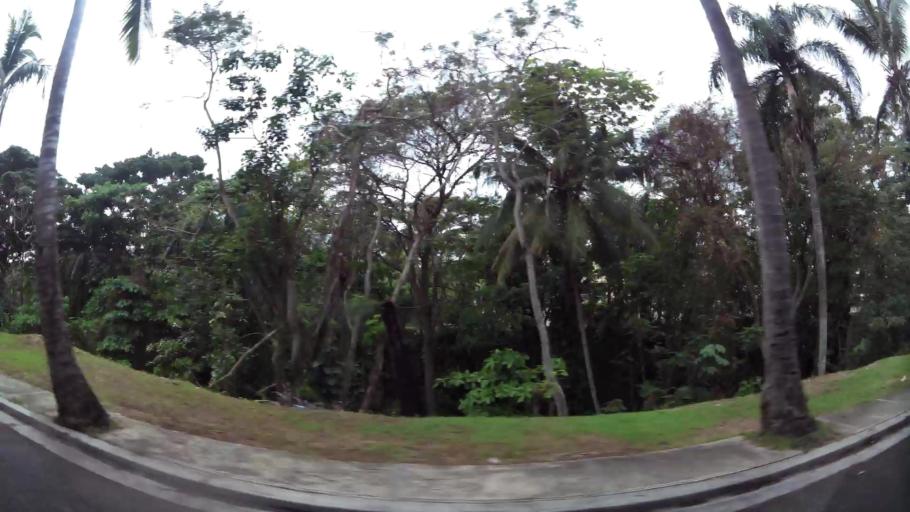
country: DO
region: Nacional
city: La Agustina
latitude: 18.5037
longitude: -69.9364
